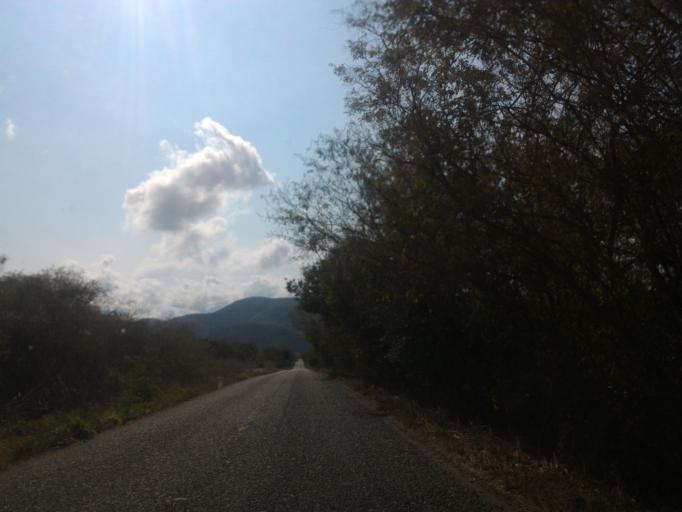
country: MX
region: Michoacan
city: Coahuayana Viejo
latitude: 18.5140
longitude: -103.5799
